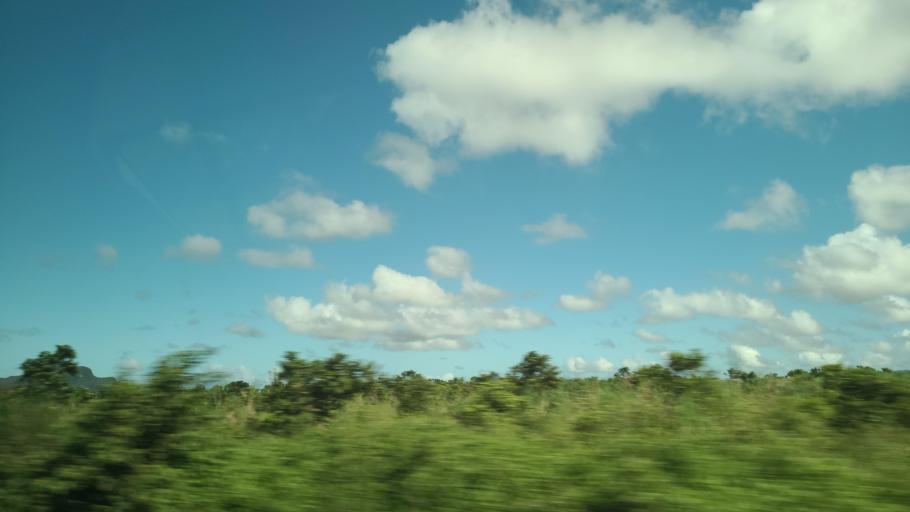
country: MU
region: Flacq
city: Saint Julien
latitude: -20.2366
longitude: 57.6310
